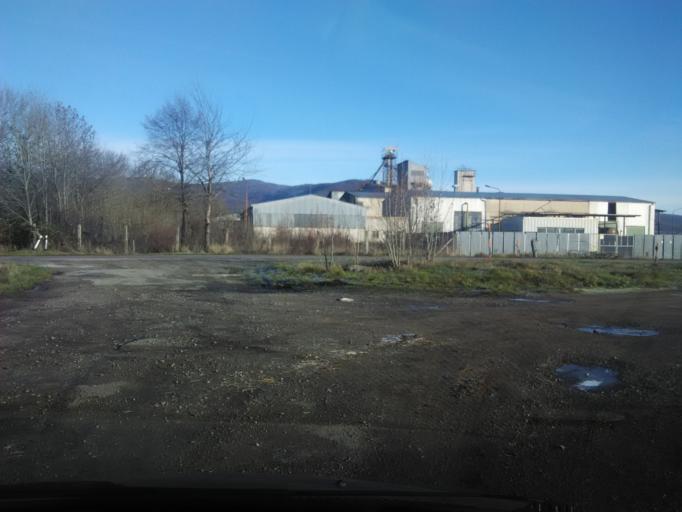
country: SK
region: Nitriansky
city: Tlmace
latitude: 48.3577
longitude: 18.5173
